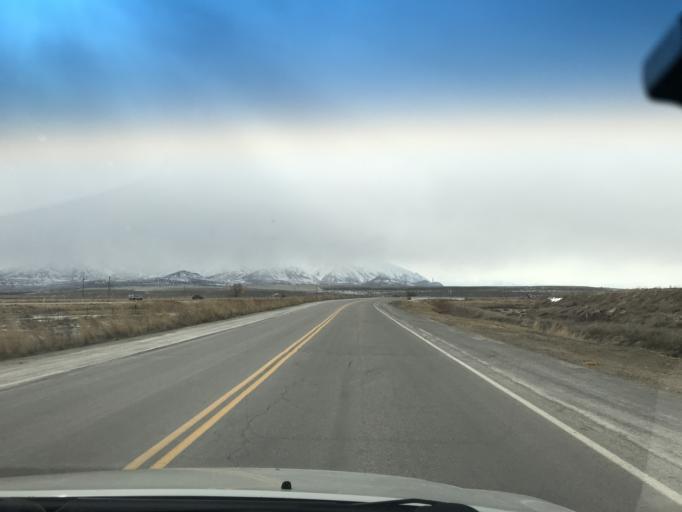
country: US
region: Utah
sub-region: Salt Lake County
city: Magna
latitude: 40.7727
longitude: -112.0656
